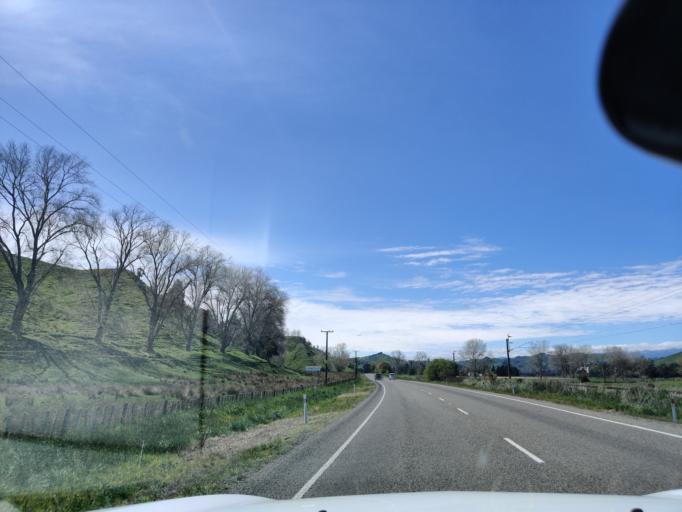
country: NZ
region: Manawatu-Wanganui
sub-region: Ruapehu District
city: Waiouru
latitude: -39.8546
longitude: 175.7265
